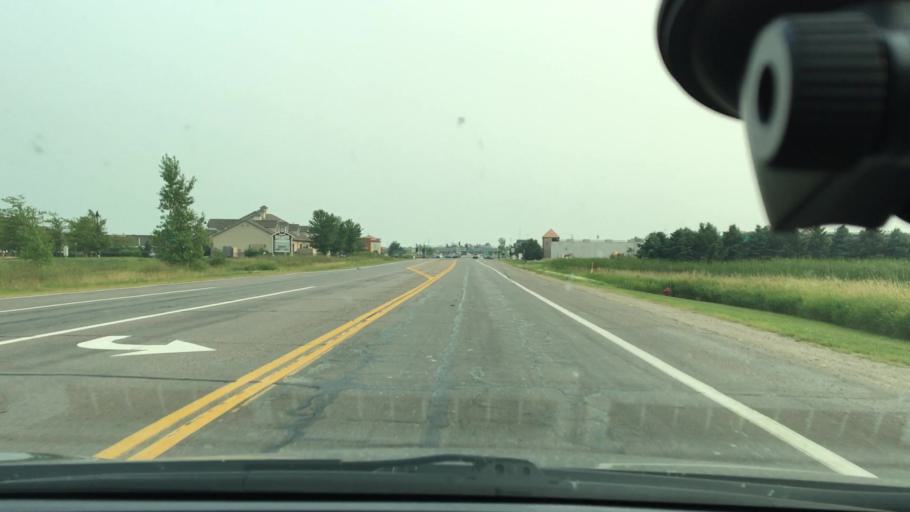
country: US
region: Minnesota
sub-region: Wright County
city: Albertville
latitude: 45.2478
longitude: -93.6633
